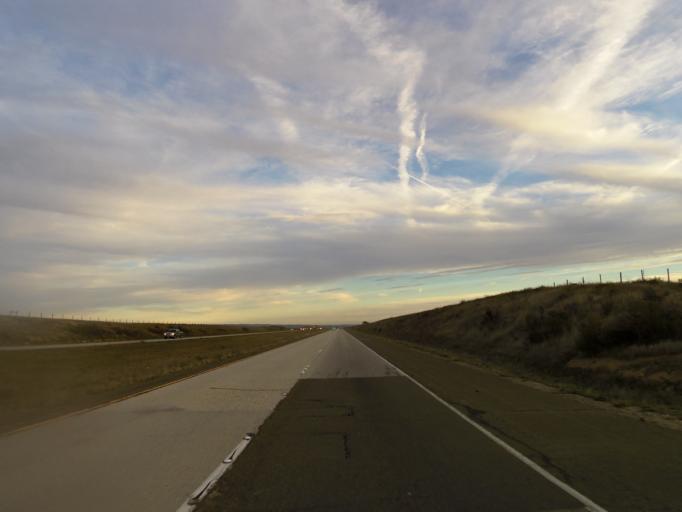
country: US
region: California
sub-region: Monterey County
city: King City
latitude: 36.0368
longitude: -120.9497
